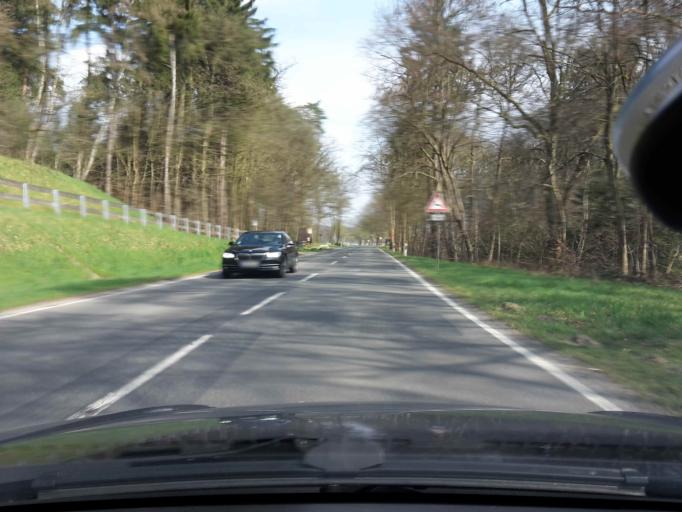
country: DE
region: Lower Saxony
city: Jesteburg
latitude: 53.2932
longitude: 9.9237
